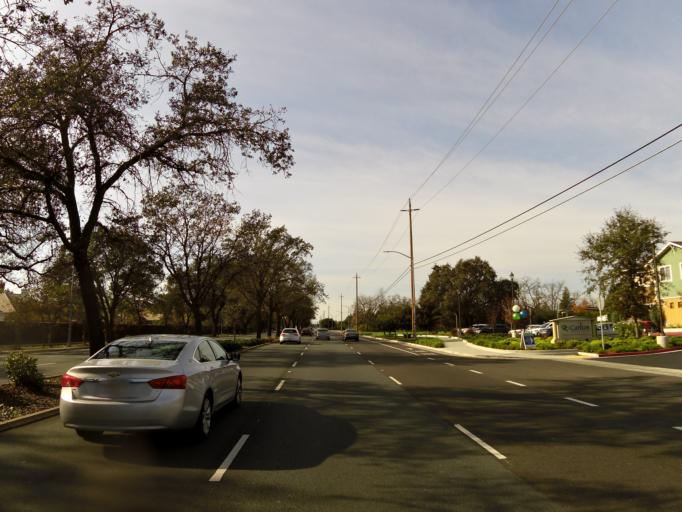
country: US
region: California
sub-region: Sacramento County
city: Laguna
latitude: 38.4090
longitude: -121.4226
